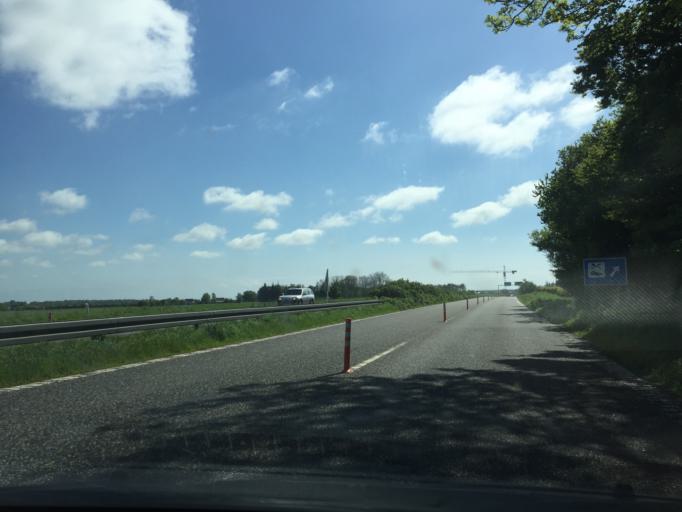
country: DK
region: Zealand
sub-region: Lolland Kommune
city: Holeby
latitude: 54.7220
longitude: 11.4331
